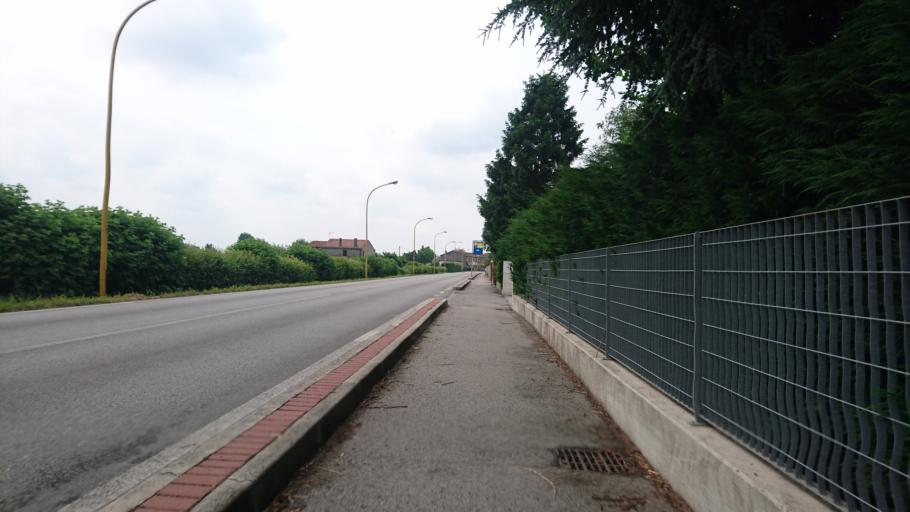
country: IT
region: Veneto
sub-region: Provincia di Padova
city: Villa Estense
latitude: 45.1783
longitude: 11.6709
